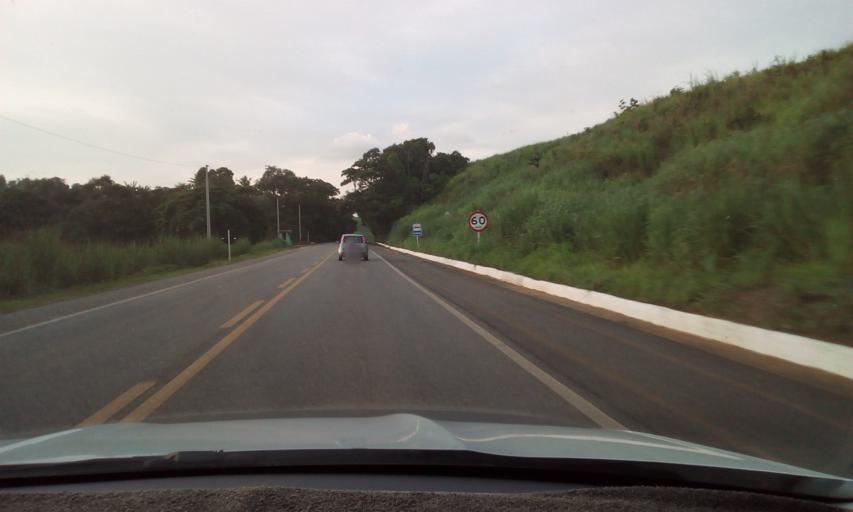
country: BR
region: Pernambuco
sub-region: Vicencia
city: Vicencia
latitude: -7.6449
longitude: -35.2537
